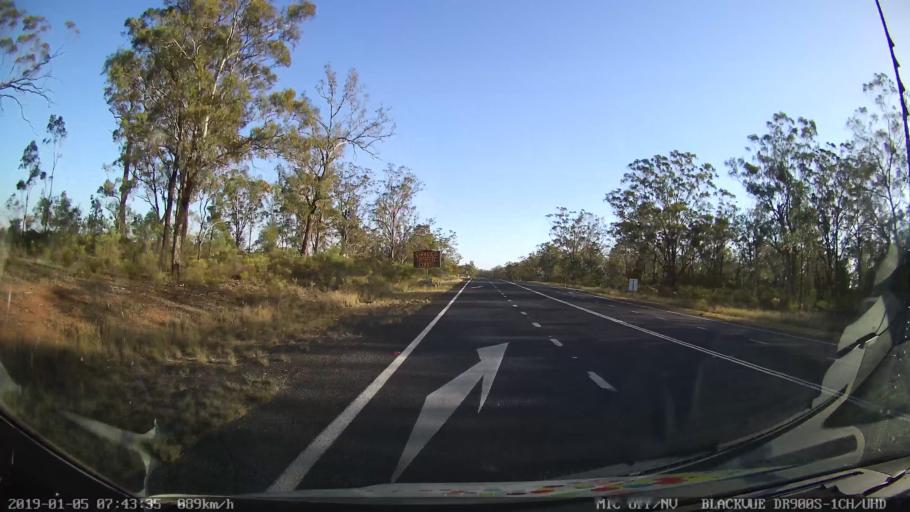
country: AU
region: New South Wales
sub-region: Gilgandra
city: Gilgandra
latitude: -31.8834
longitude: 148.6348
